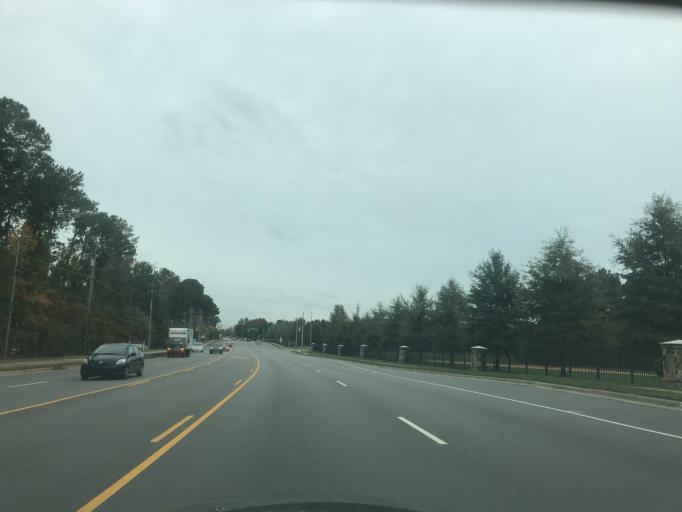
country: US
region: North Carolina
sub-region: Wake County
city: West Raleigh
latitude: 35.8868
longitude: -78.6276
